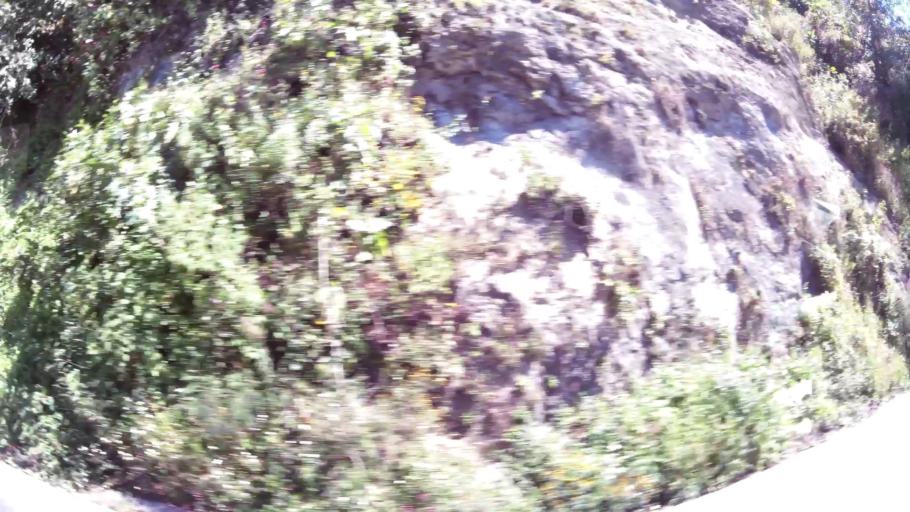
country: GT
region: Solola
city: Solola
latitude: 14.7597
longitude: -91.1758
